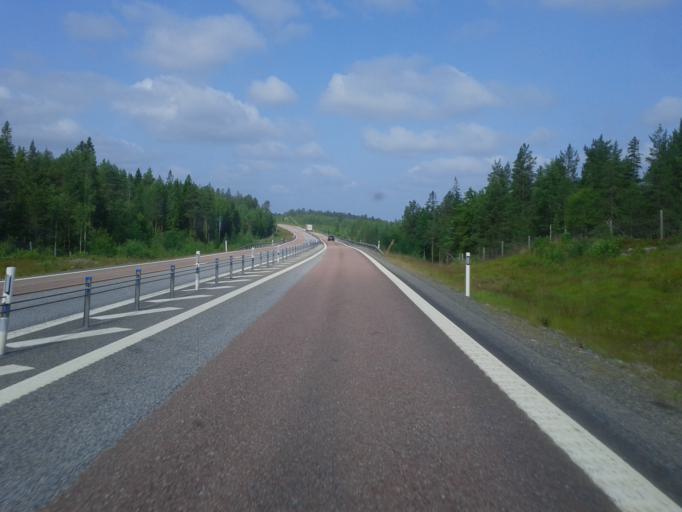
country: SE
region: Vaesterbotten
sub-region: Skelleftea Kommun
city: Soedra Bergsbyn
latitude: 64.6830
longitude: 21.0669
